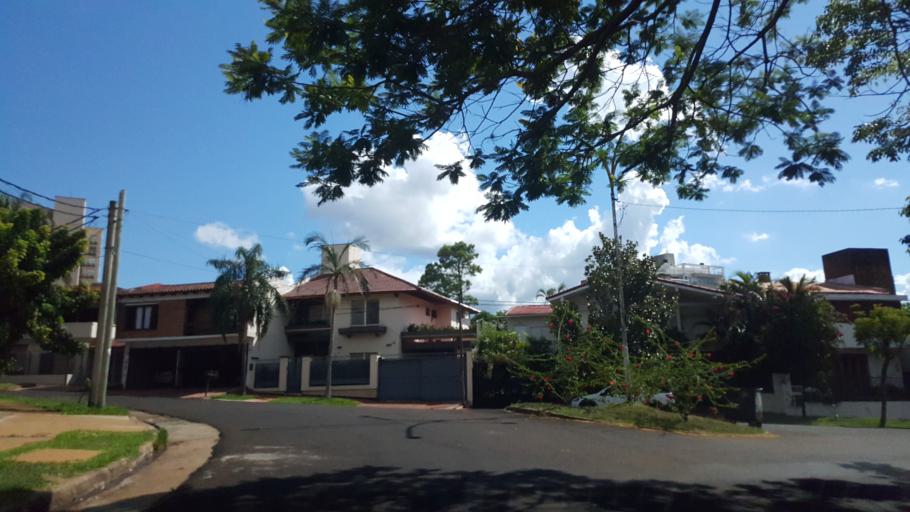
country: AR
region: Misiones
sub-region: Departamento de Capital
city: Posadas
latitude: -27.3531
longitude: -55.8963
